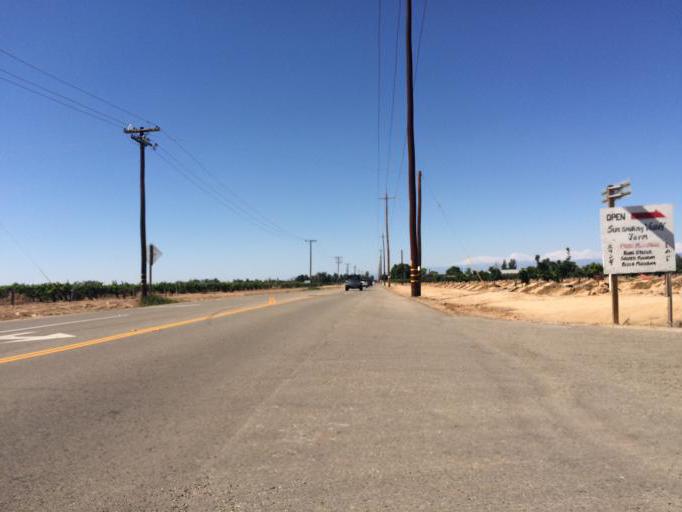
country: US
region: California
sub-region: Fresno County
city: Sanger
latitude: 36.7372
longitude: -119.6100
